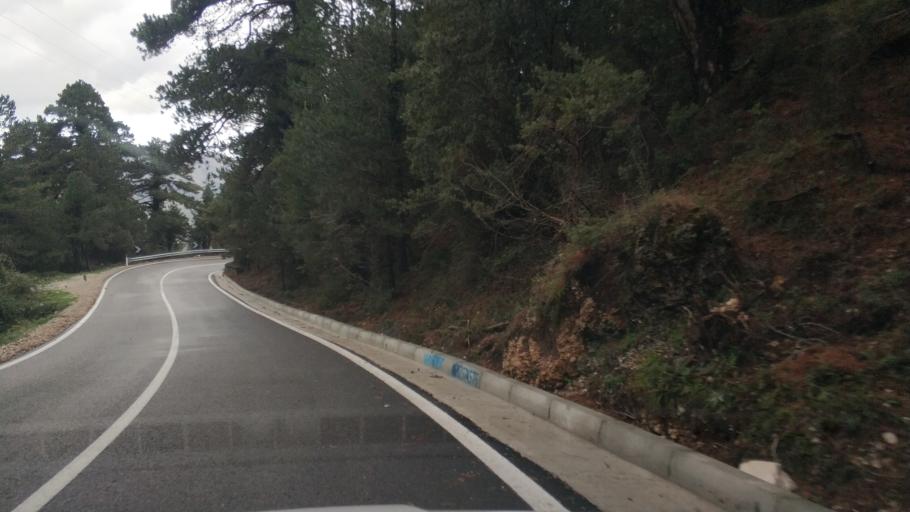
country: AL
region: Vlore
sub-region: Rrethi i Vlores
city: Brataj
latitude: 40.2181
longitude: 19.5792
